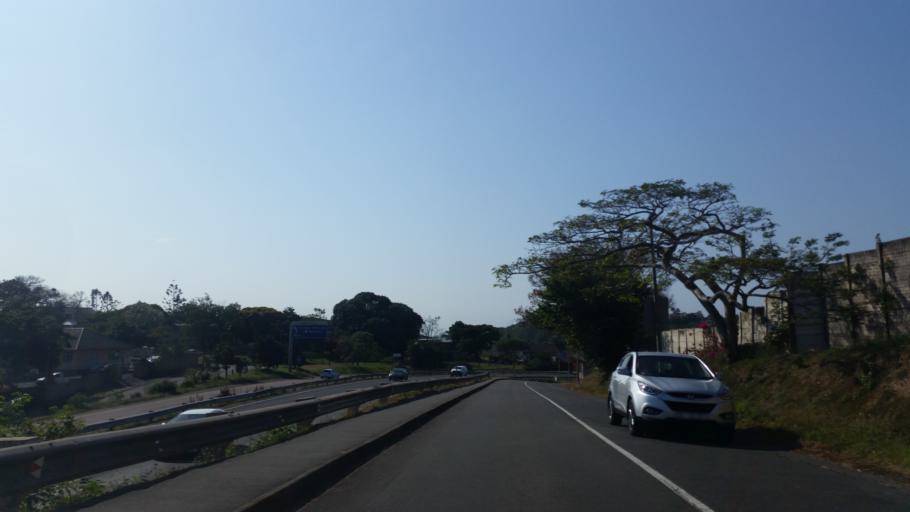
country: ZA
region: KwaZulu-Natal
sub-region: eThekwini Metropolitan Municipality
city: Berea
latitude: -29.8351
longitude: 30.9110
